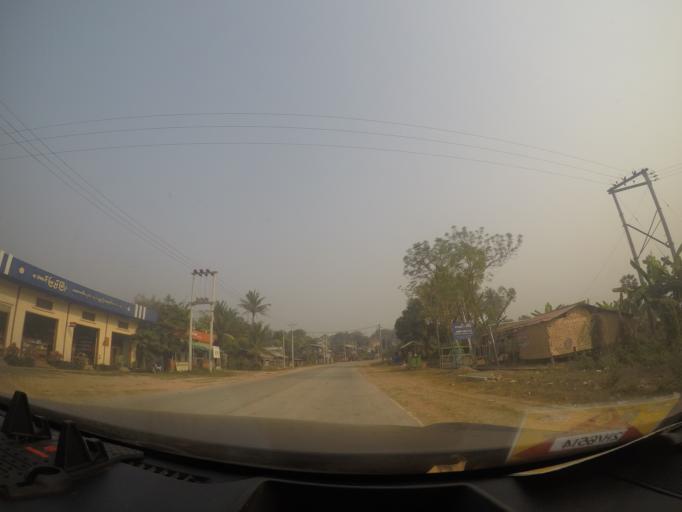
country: MM
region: Mandalay
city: Nay Pyi Taw
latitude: 19.9057
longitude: 96.0241
